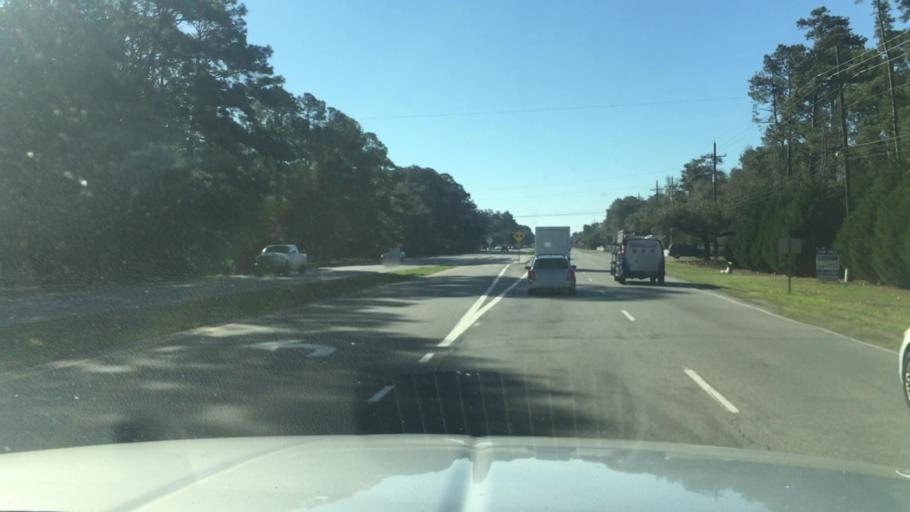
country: US
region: North Carolina
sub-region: New Hanover County
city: Sea Breeze
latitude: 34.0924
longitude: -77.8972
